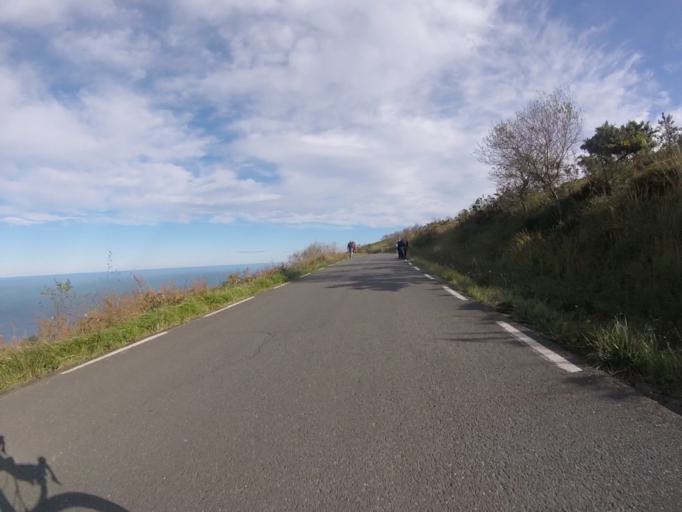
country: ES
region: Basque Country
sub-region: Provincia de Guipuzcoa
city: Usurbil
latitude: 43.2963
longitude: -2.0766
